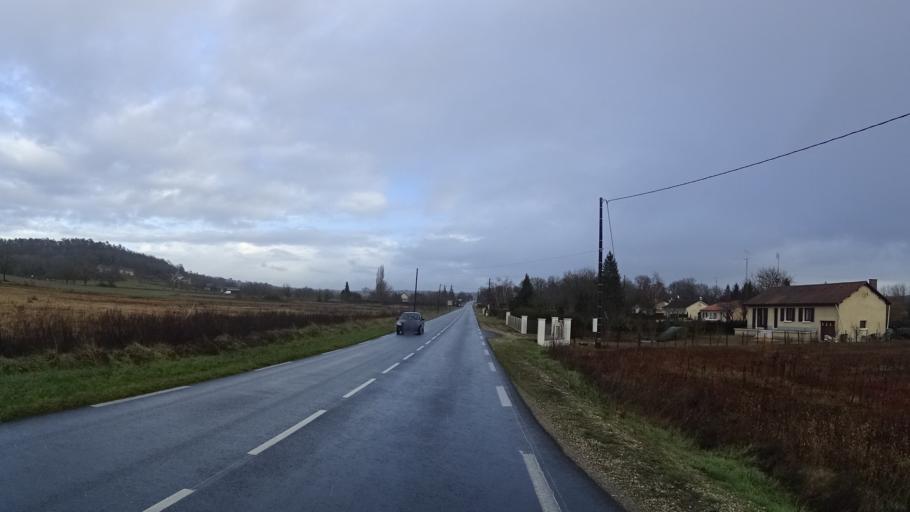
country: FR
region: Aquitaine
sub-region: Departement de la Dordogne
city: Sorges
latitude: 45.2970
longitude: 0.9535
